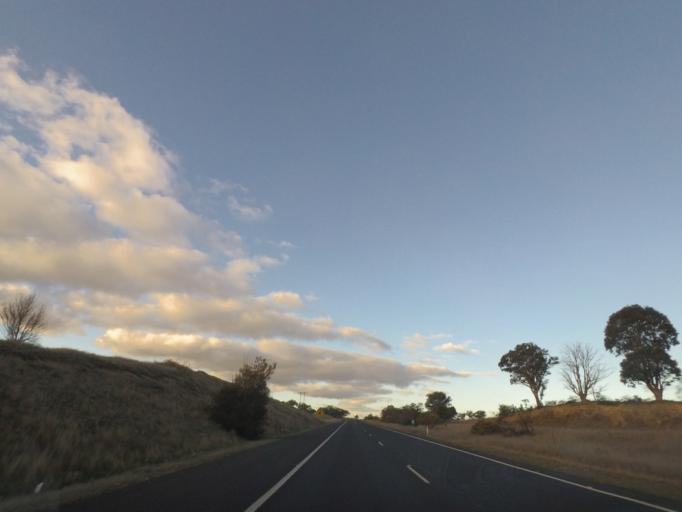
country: AU
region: New South Wales
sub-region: Yass Valley
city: Yass
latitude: -34.7687
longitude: 148.7501
